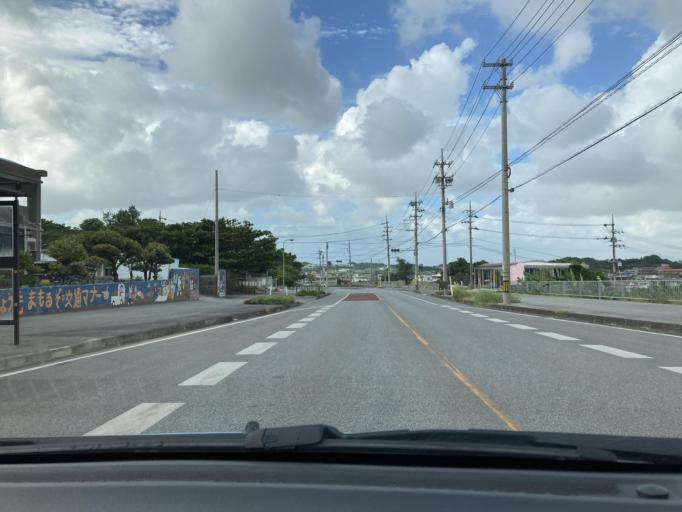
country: JP
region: Okinawa
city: Itoman
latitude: 26.1263
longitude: 127.6915
